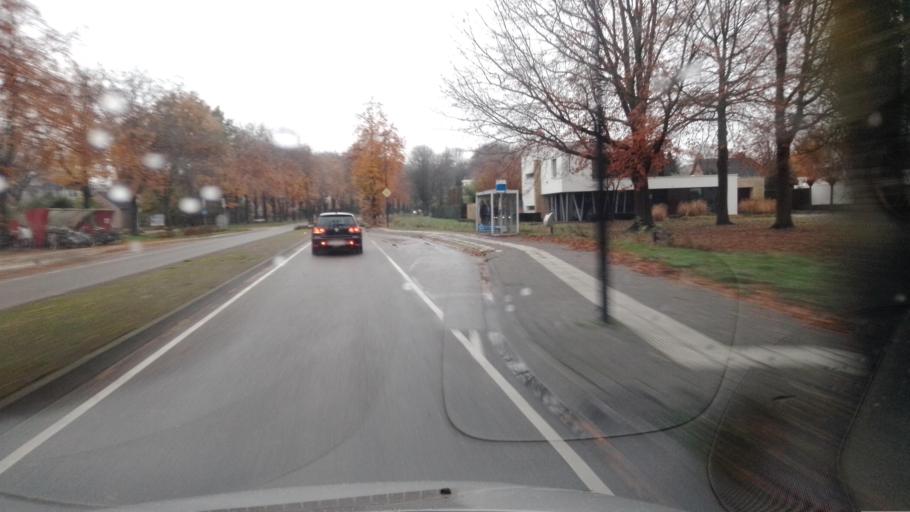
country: NL
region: North Brabant
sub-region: Gemeente Asten
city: Asten
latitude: 51.4091
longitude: 5.7563
